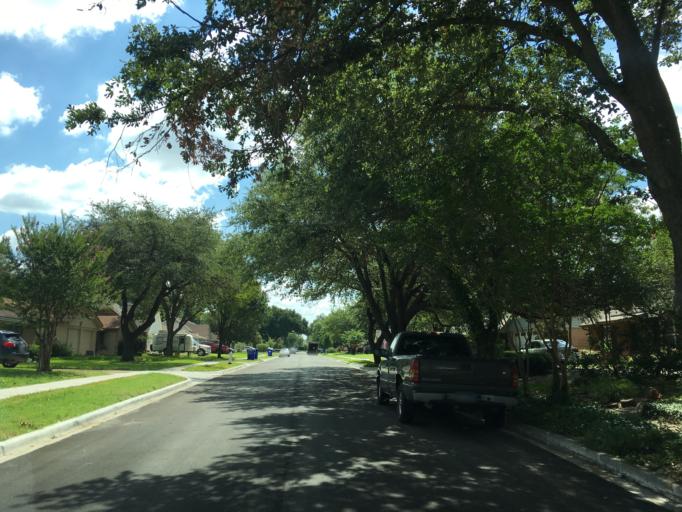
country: US
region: Texas
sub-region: Dallas County
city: Farmers Branch
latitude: 32.9283
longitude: -96.8789
